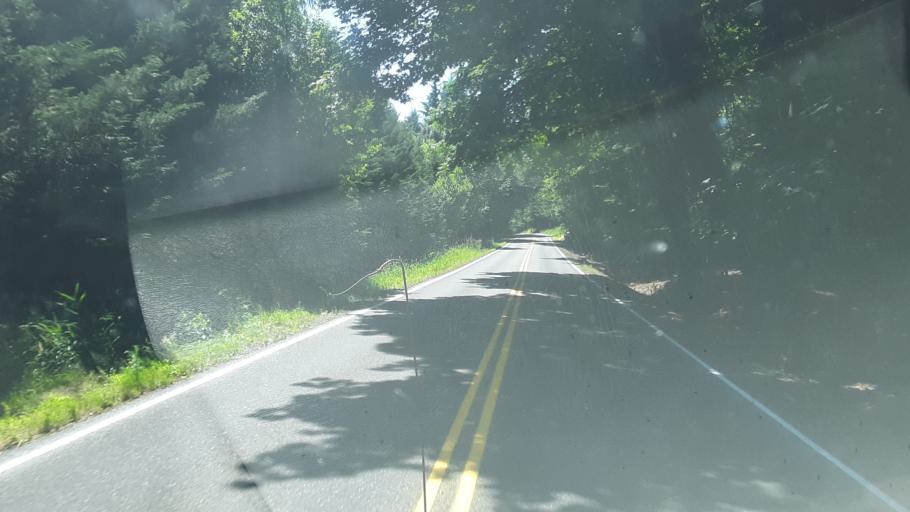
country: US
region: Washington
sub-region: Clark County
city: Amboy
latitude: 45.9232
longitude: -122.4296
